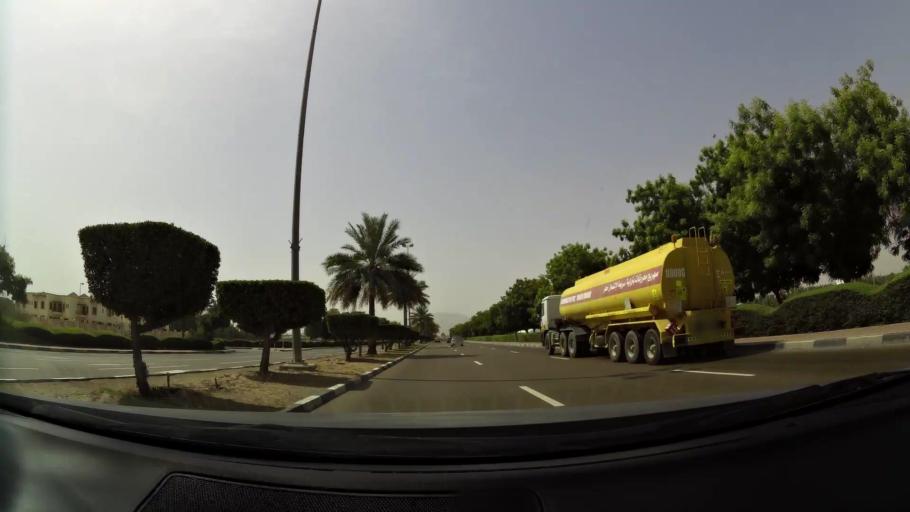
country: AE
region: Abu Dhabi
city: Al Ain
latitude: 24.1738
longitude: 55.7077
